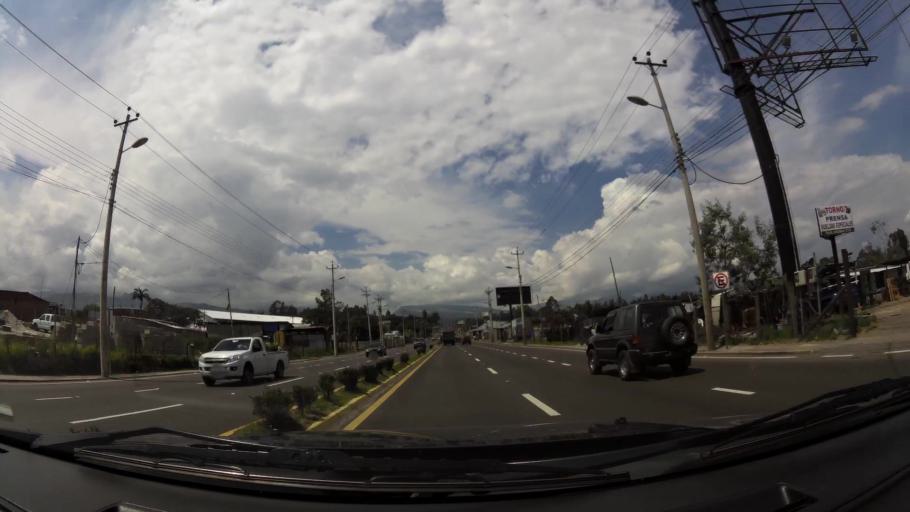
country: EC
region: Pichincha
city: Sangolqui
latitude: -0.2109
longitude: -78.3637
